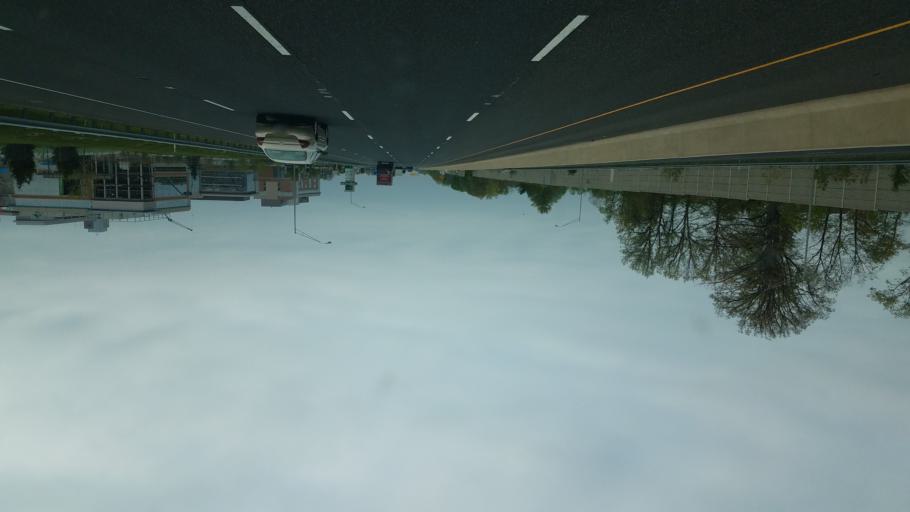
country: US
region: Indiana
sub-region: Allen County
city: Fort Wayne
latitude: 41.1818
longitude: -85.1035
